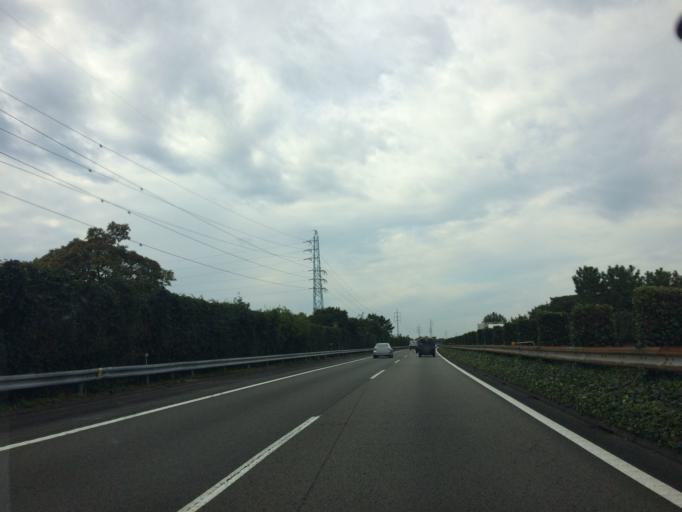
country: JP
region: Shizuoka
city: Fujieda
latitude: 34.8353
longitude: 138.2793
